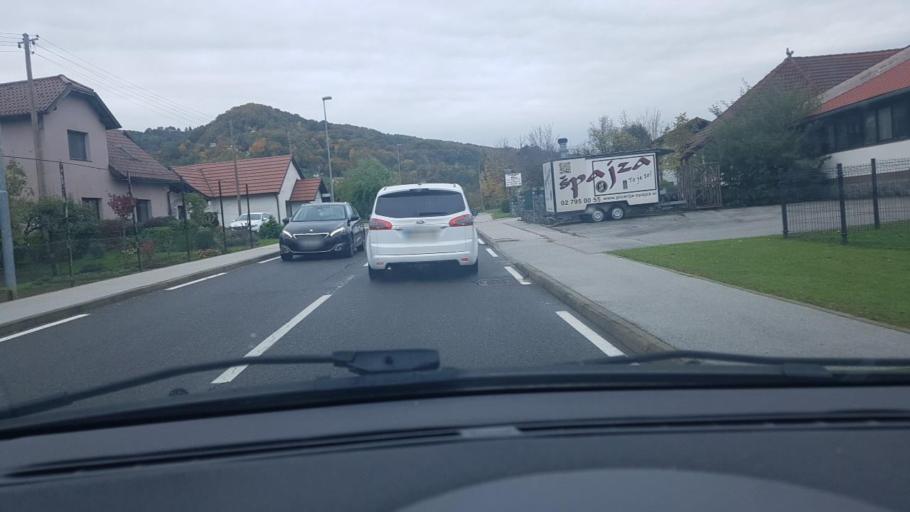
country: SI
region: Majsperk
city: Majsperk
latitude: 46.3369
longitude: 15.7368
